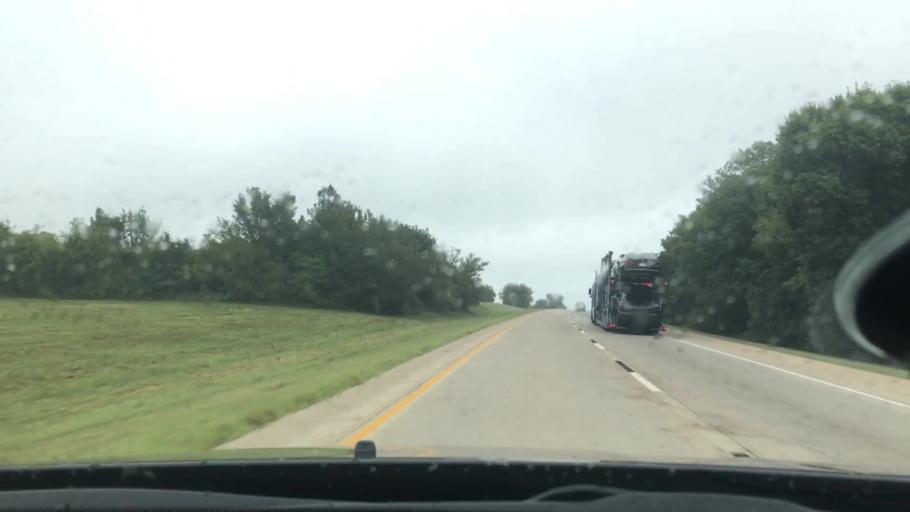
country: US
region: Oklahoma
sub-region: Okmulgee County
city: Henryetta
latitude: 35.4326
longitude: -95.9340
